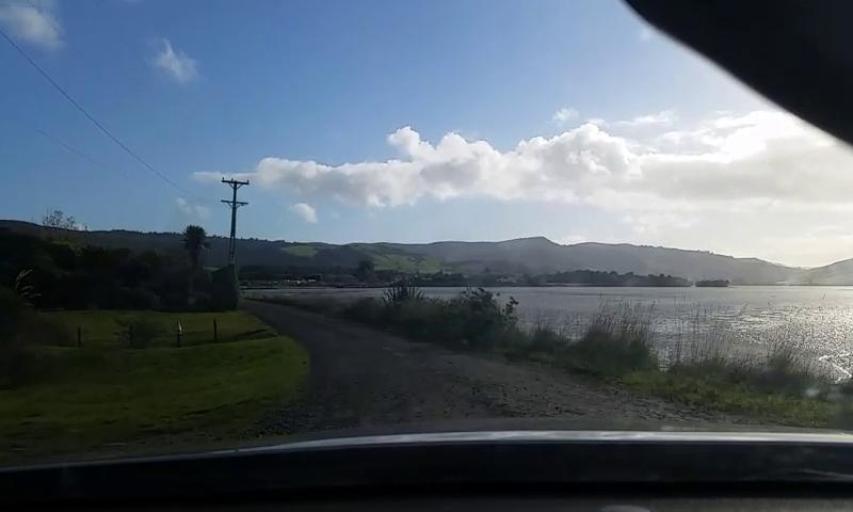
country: NZ
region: Otago
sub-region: Clutha District
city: Papatowai
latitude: -46.6302
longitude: 169.1408
